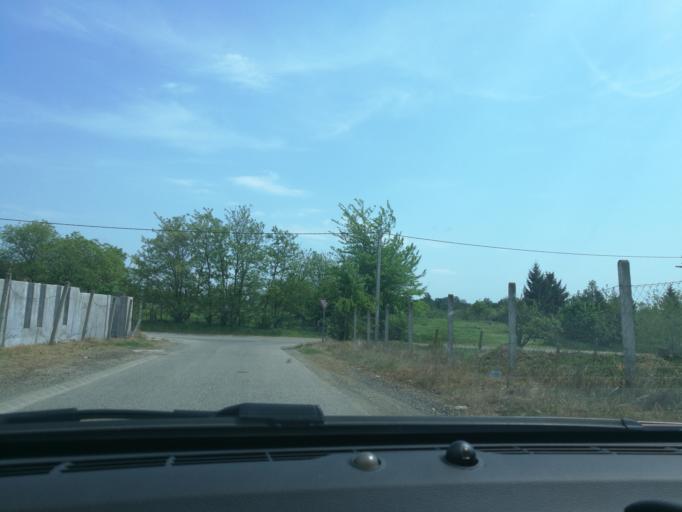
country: HU
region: Szabolcs-Szatmar-Bereg
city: Nyiregyhaza
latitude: 47.9628
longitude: 21.6843
